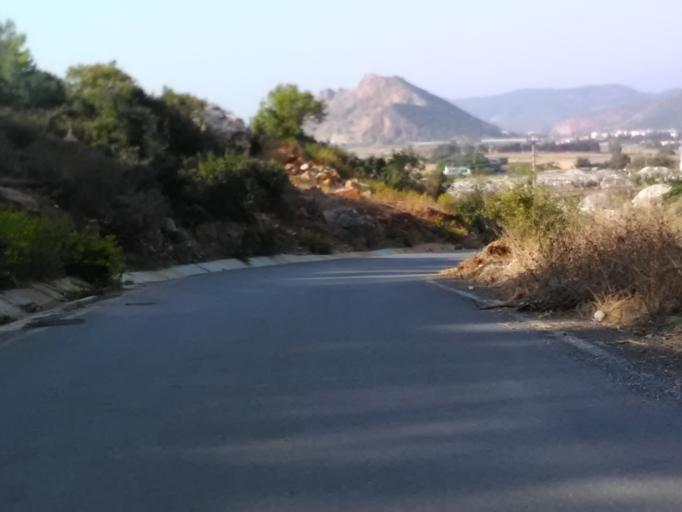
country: TR
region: Antalya
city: Gazipasa
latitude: 36.2342
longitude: 32.3006
